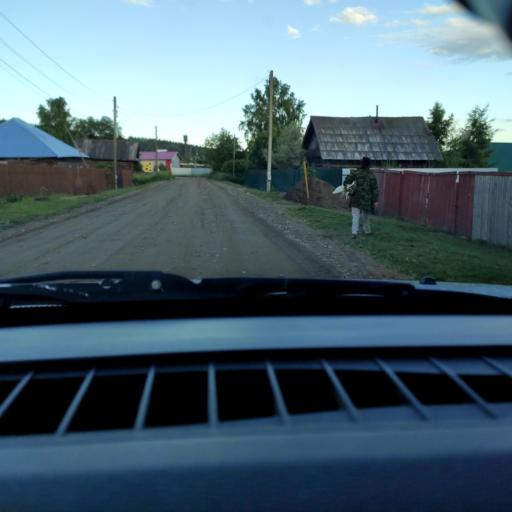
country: RU
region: Perm
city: Novyye Lyady
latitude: 58.1739
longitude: 56.5523
